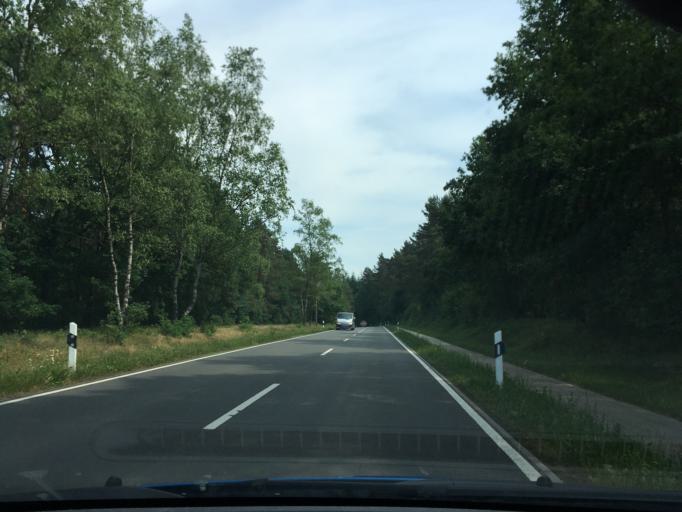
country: DE
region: Lower Saxony
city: Asendorf
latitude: 53.2680
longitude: 9.9602
